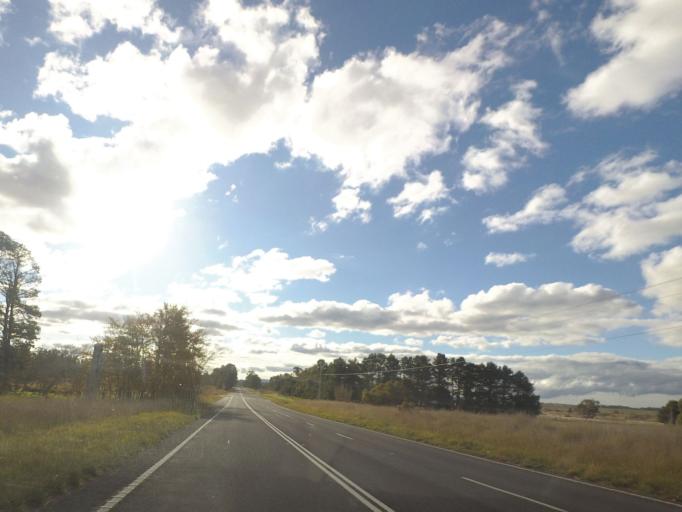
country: AU
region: Victoria
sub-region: Mount Alexander
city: Castlemaine
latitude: -37.1569
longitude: 144.3551
